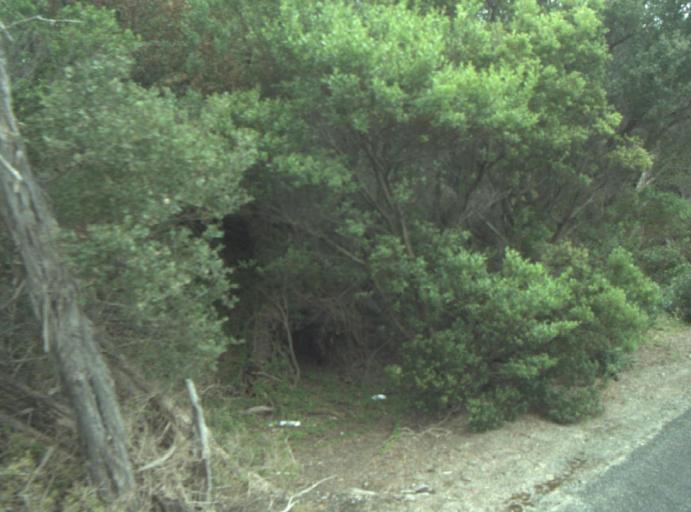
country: AU
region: Victoria
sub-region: Queenscliffe
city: Queenscliff
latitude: -38.2677
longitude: 144.6054
